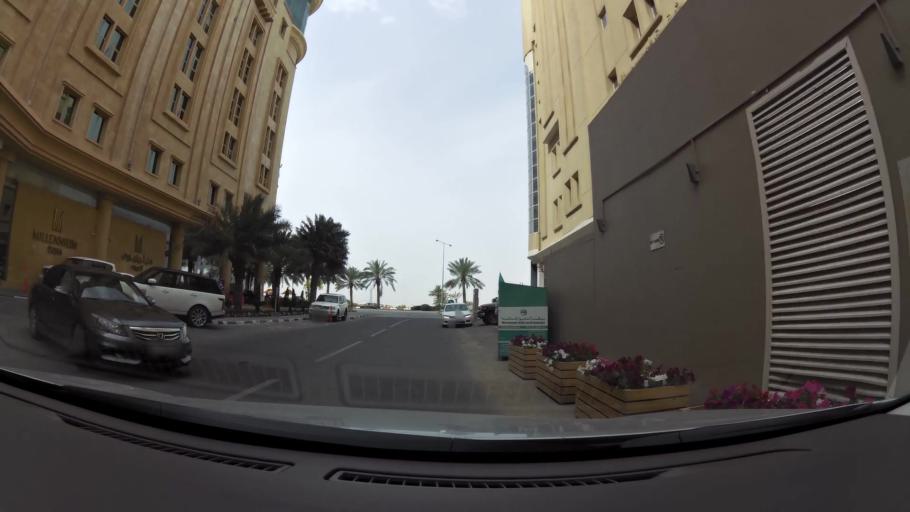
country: QA
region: Baladiyat ad Dawhah
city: Doha
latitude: 25.2836
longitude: 51.4958
